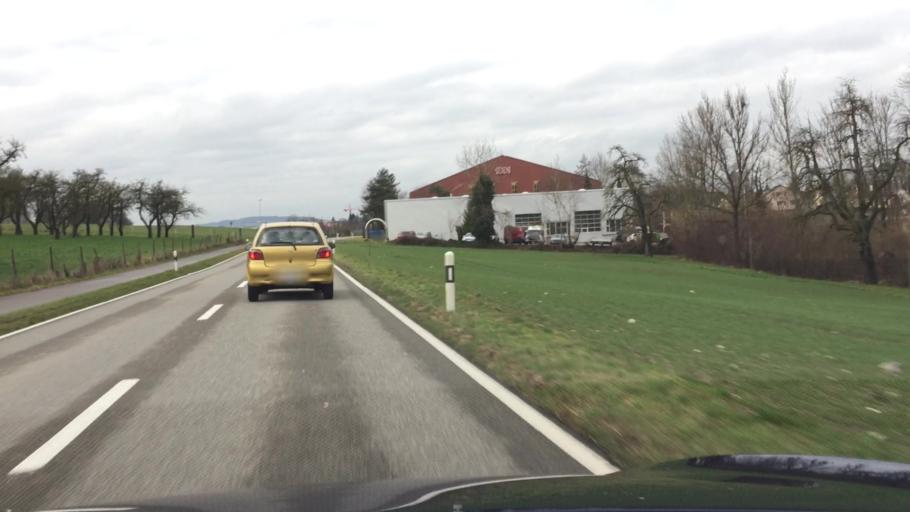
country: CH
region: Thurgau
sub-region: Arbon District
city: Amriswil
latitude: 47.5398
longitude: 9.2918
